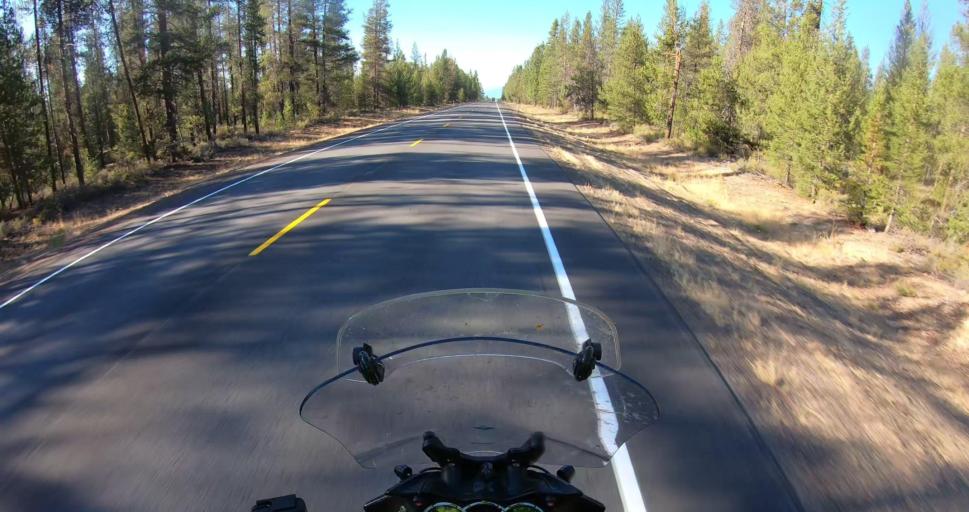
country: US
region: Oregon
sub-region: Deschutes County
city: La Pine
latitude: 43.5554
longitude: -121.4740
